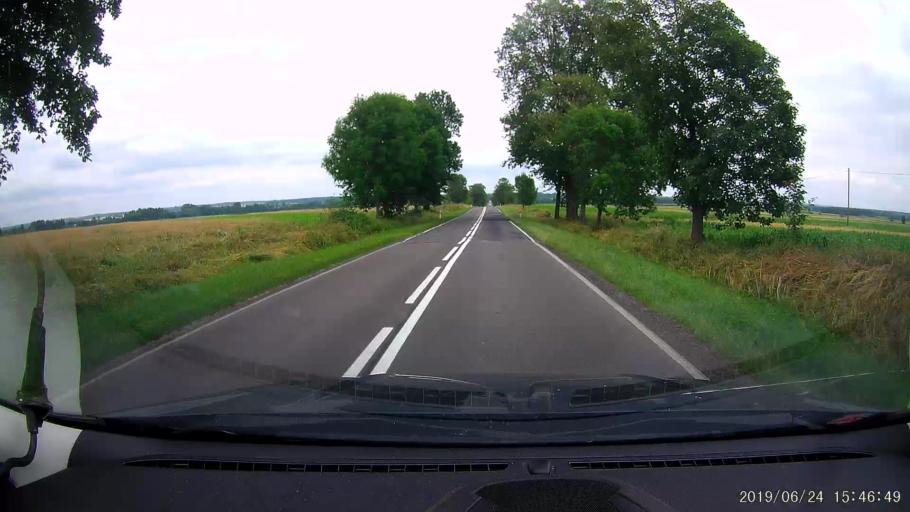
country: PL
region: Subcarpathian Voivodeship
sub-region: Powiat lubaczowski
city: Oleszyce
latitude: 50.1580
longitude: 23.0066
